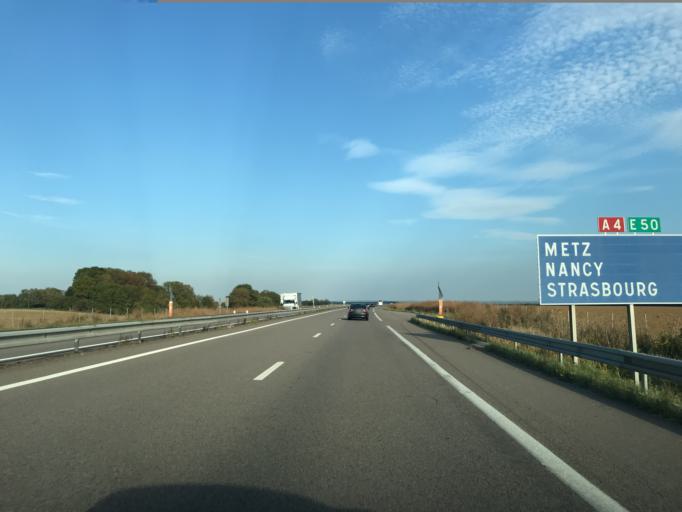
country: FR
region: Lorraine
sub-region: Departement de la Meuse
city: Etain
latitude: 49.1274
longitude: 5.6390
